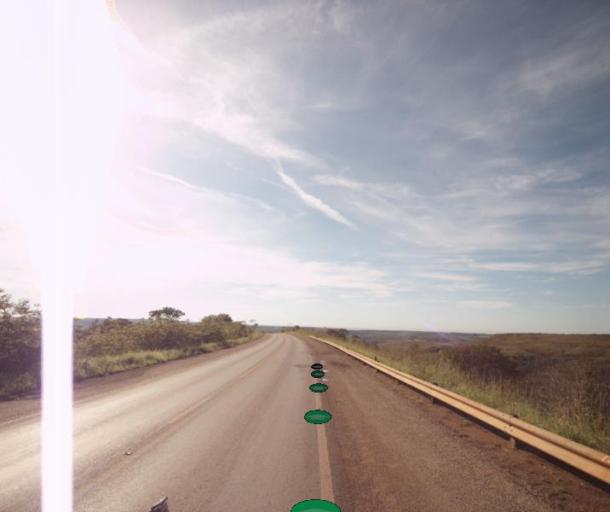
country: BR
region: Federal District
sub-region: Brasilia
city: Brasilia
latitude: -15.7417
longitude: -48.3812
